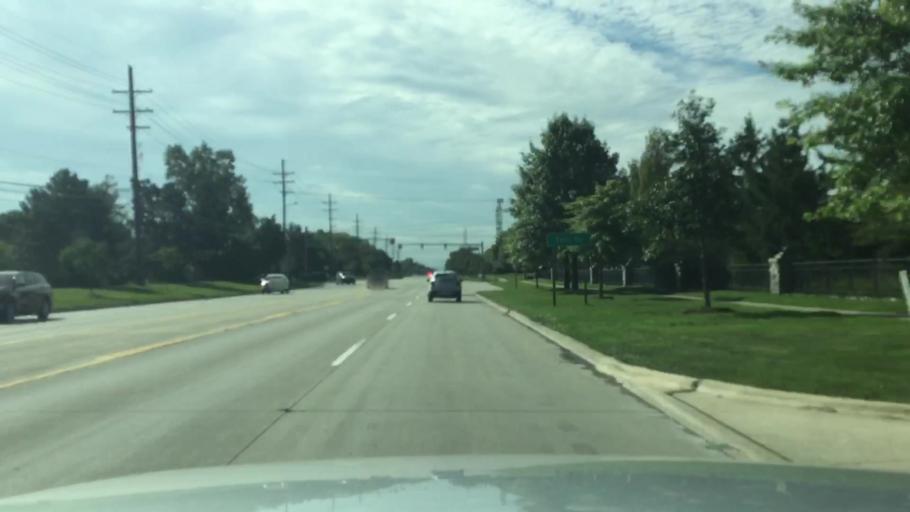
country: US
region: Michigan
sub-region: Wayne County
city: Canton
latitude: 42.3160
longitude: -83.4877
